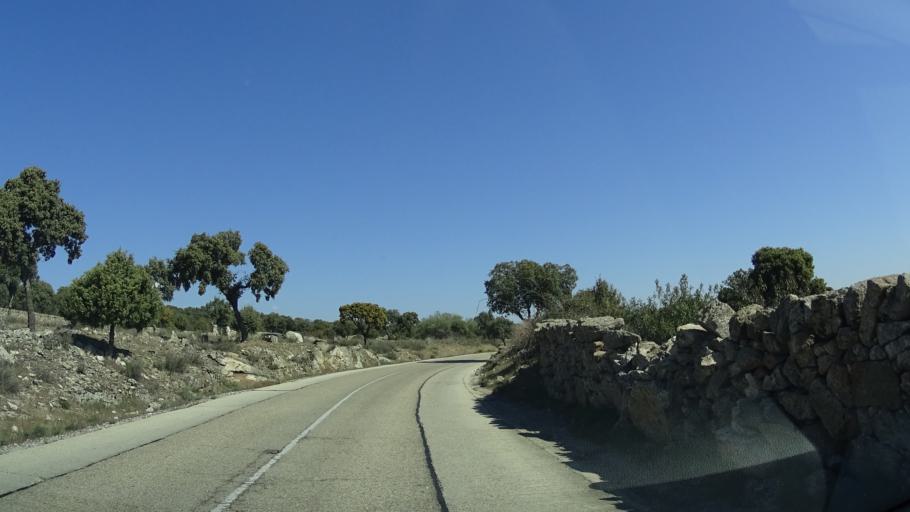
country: ES
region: Madrid
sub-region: Provincia de Madrid
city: Hoyo de Manzanares
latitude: 40.6410
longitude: -3.8475
